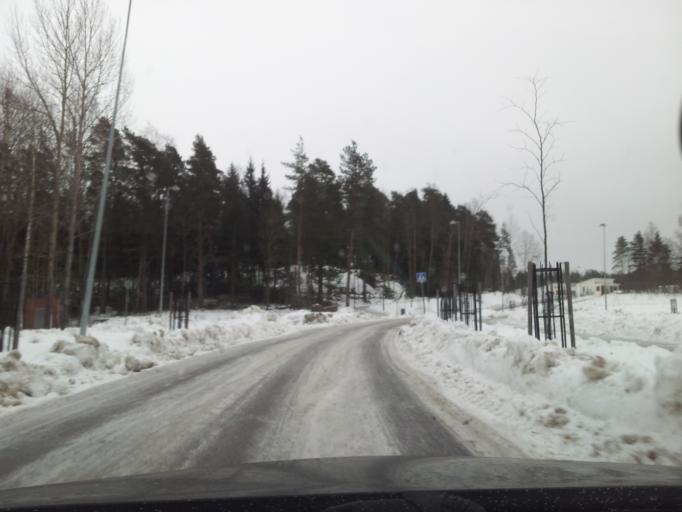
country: FI
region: Uusimaa
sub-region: Helsinki
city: Espoo
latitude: 60.1605
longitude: 24.5586
